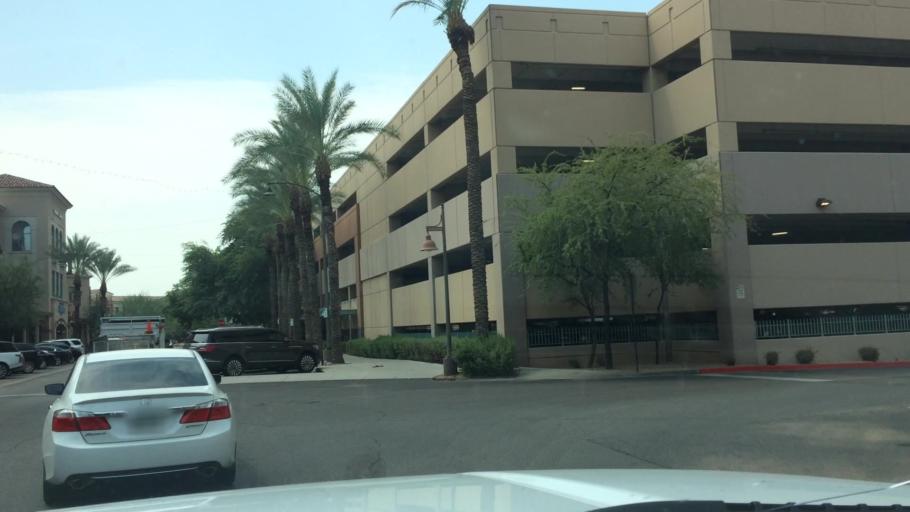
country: US
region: Arizona
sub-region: Maricopa County
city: Scottsdale
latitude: 33.5013
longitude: -111.9287
